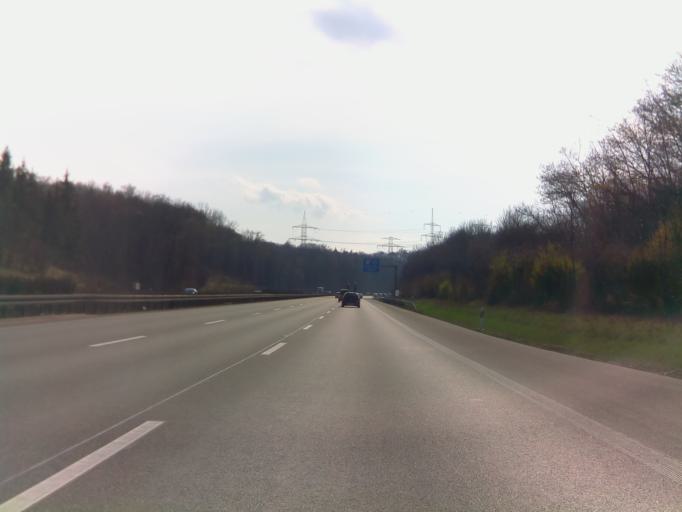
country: DE
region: Thuringia
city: Klettbach
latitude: 50.9361
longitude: 11.1514
